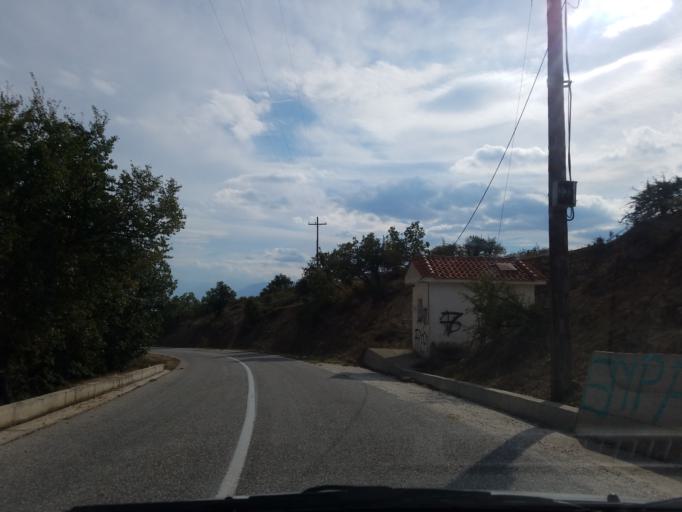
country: GR
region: Thessaly
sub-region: Trikala
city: Kastraki
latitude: 39.7433
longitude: 21.6573
